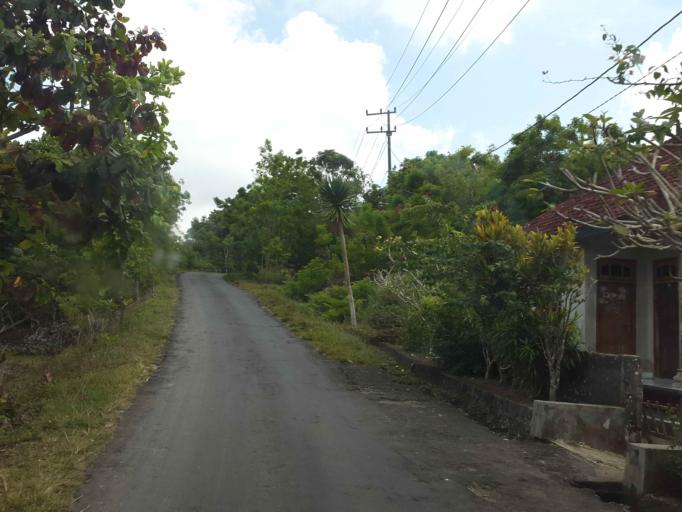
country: ID
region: Bali
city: Klumbu
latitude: -8.7328
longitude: 115.5436
